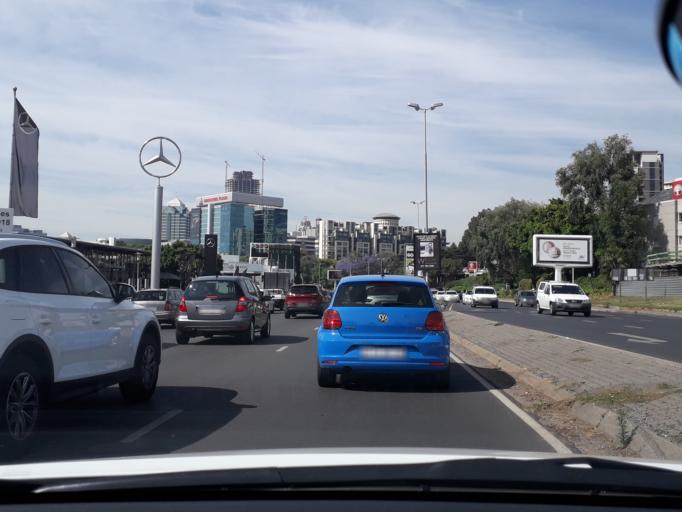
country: ZA
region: Gauteng
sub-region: City of Johannesburg Metropolitan Municipality
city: Modderfontein
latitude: -26.0925
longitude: 28.0565
